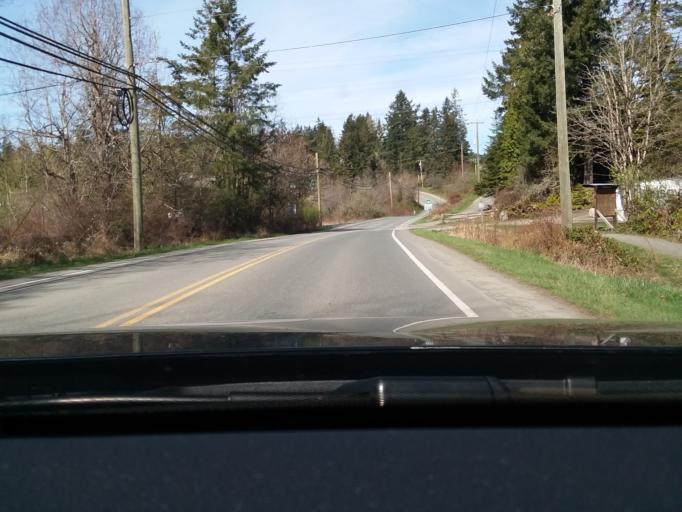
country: CA
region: British Columbia
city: North Cowichan
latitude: 48.8640
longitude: -123.5013
